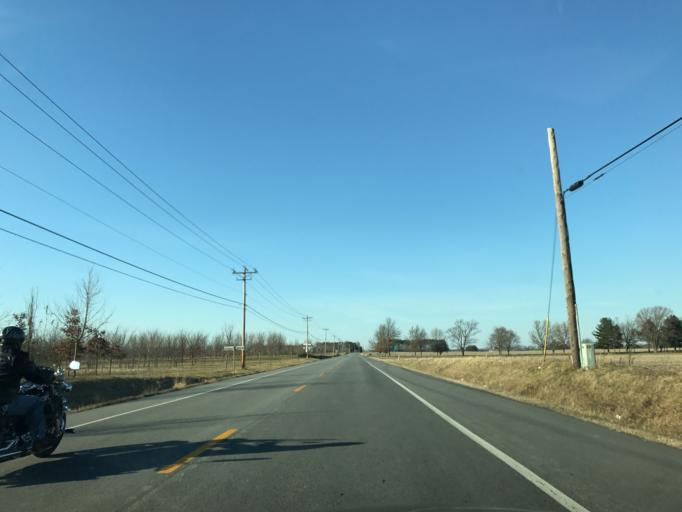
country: US
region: Maryland
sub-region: Queen Anne's County
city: Kingstown
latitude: 39.1927
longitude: -75.8605
